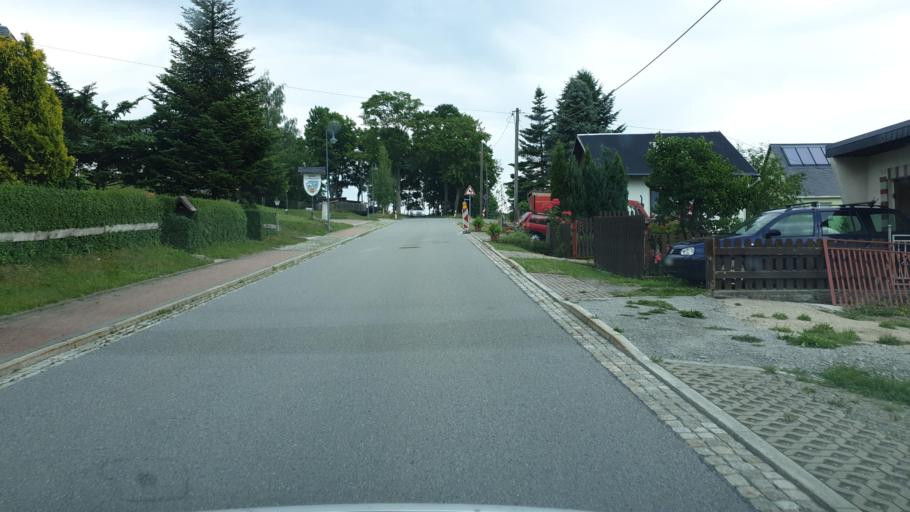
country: DE
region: Saxony
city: Elterlein
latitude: 50.5809
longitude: 12.8600
